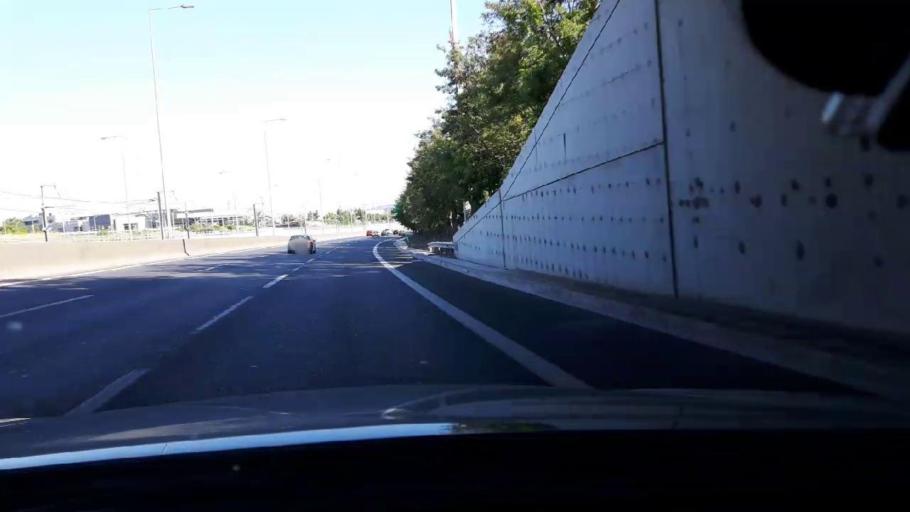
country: GR
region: Attica
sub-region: Nomarchia Anatolikis Attikis
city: Pallini
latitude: 38.0049
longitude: 23.8697
